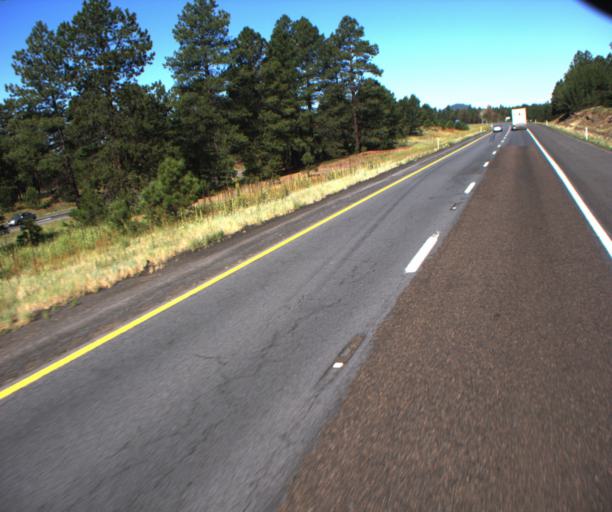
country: US
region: Arizona
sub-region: Coconino County
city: Parks
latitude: 35.2562
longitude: -111.9217
